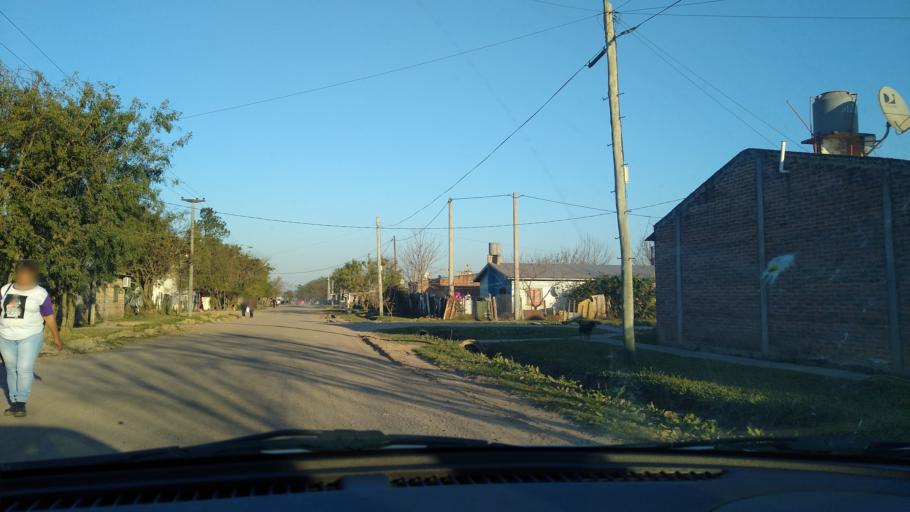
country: AR
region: Chaco
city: Resistencia
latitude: -27.4939
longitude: -58.9741
